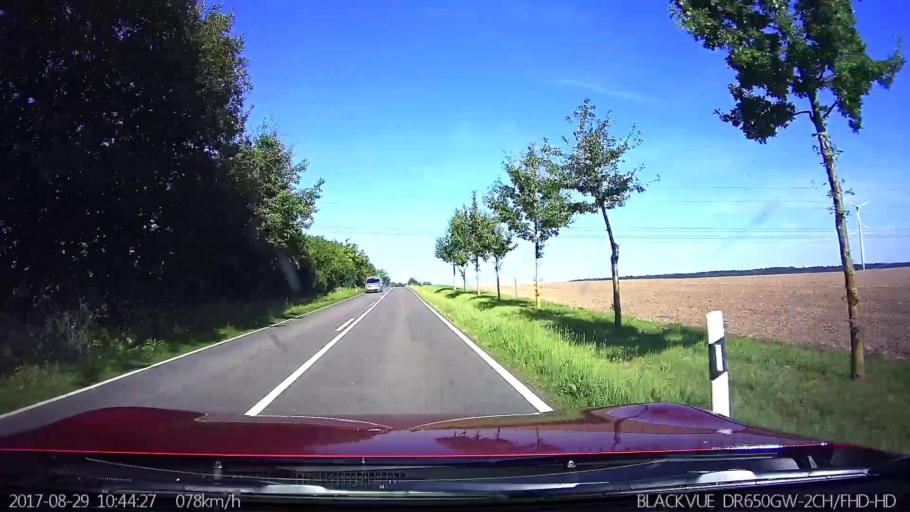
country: DE
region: Mecklenburg-Vorpommern
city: Richtenberg
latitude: 54.2030
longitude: 12.8776
